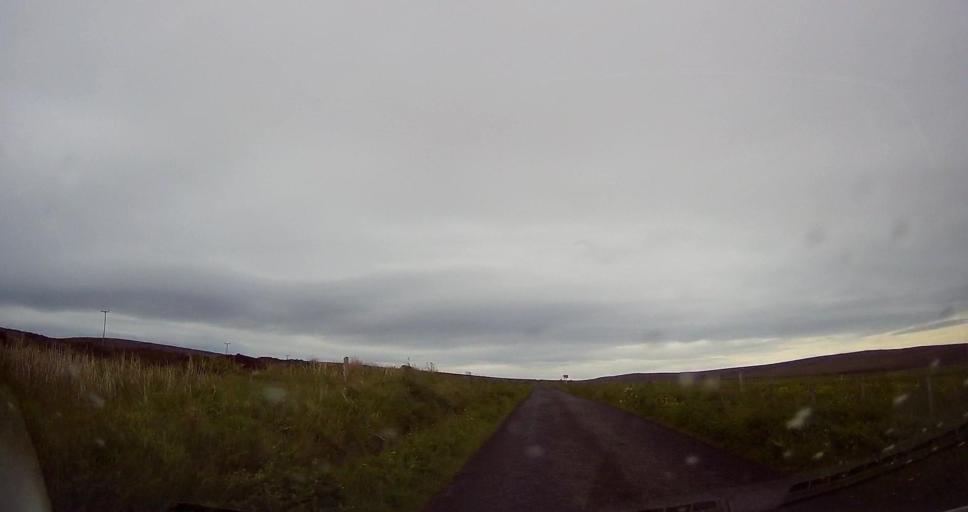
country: GB
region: Scotland
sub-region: Orkney Islands
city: Stromness
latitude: 59.0929
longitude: -3.1826
